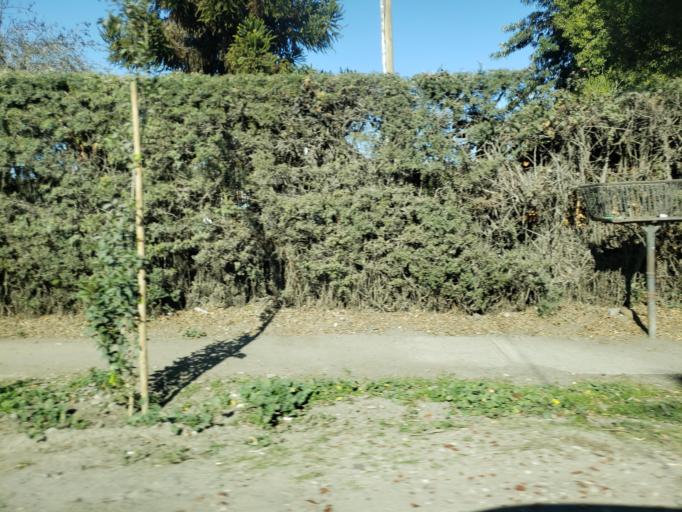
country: CL
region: Santiago Metropolitan
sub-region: Provincia de Talagante
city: El Monte
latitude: -33.6849
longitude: -71.0122
